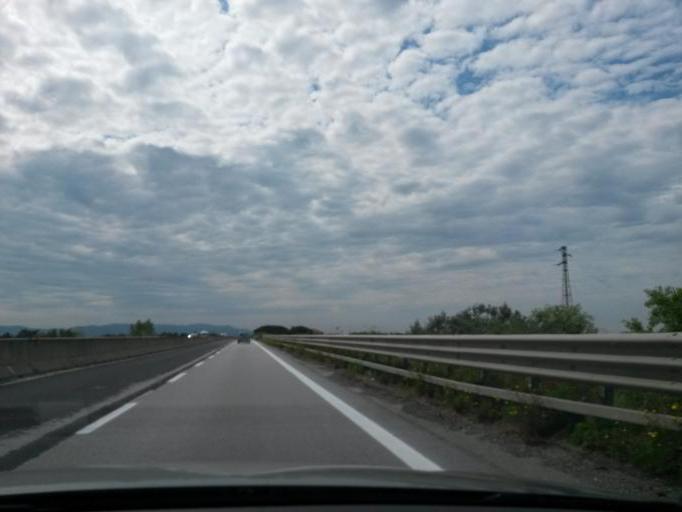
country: IT
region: Tuscany
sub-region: Provincia di Livorno
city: La California
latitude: 43.2699
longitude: 10.5405
